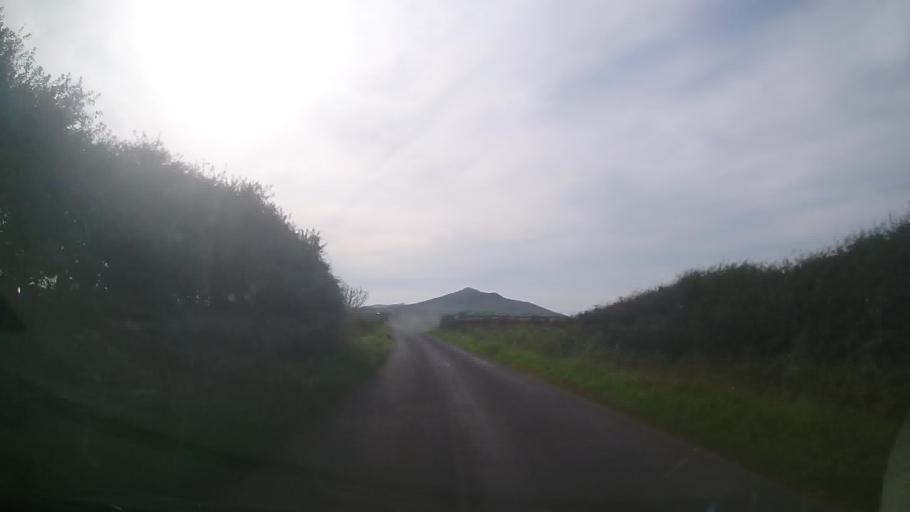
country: GB
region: Wales
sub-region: Pembrokeshire
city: Llanrhian
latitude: 51.9204
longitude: -5.2259
